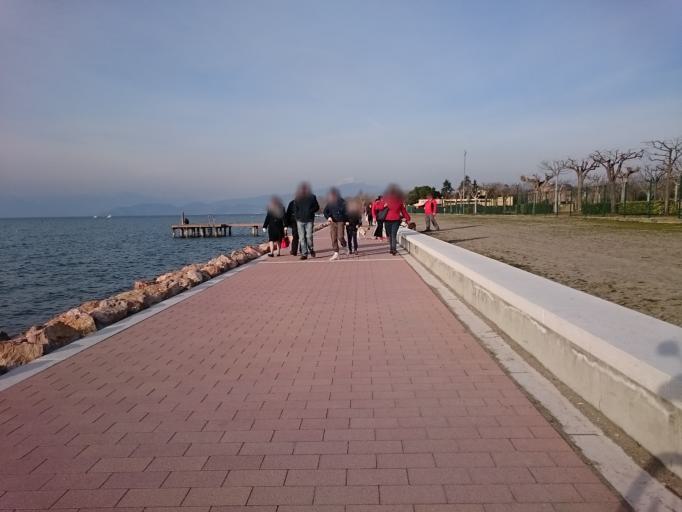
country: IT
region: Veneto
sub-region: Provincia di Verona
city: Peschiera del Garda
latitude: 45.4498
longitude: 10.6962
